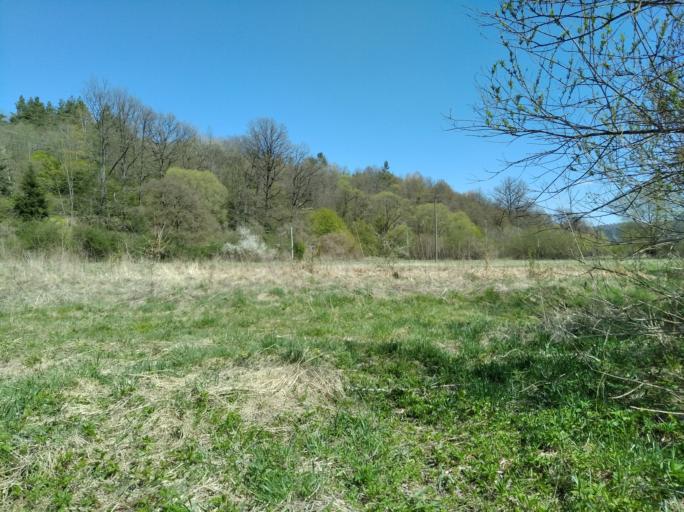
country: PL
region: Subcarpathian Voivodeship
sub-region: Powiat brzozowski
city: Dydnia
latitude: 49.7131
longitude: 22.2057
